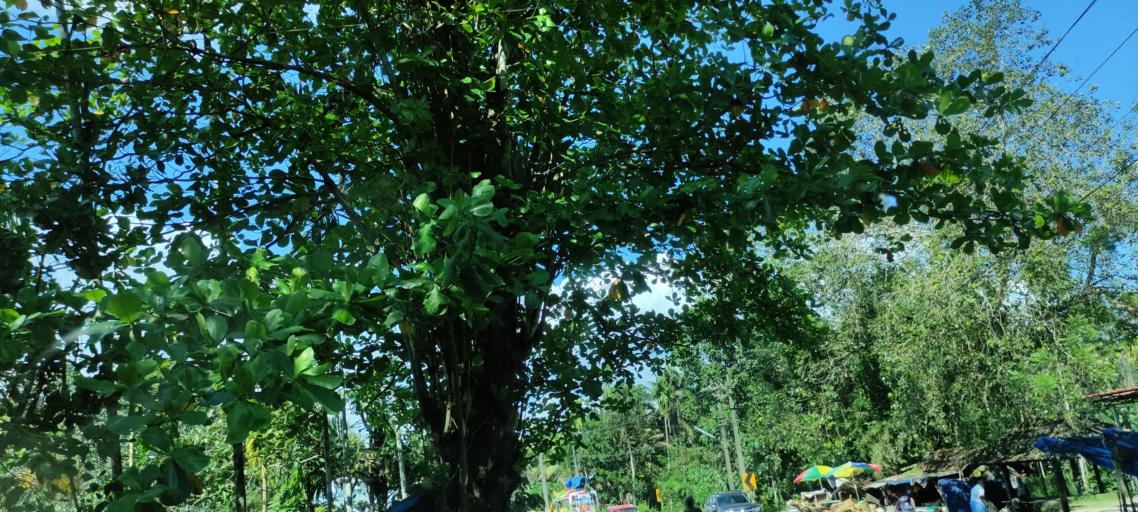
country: IN
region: Kerala
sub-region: Pattanamtitta
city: Adur
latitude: 9.1965
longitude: 76.7448
